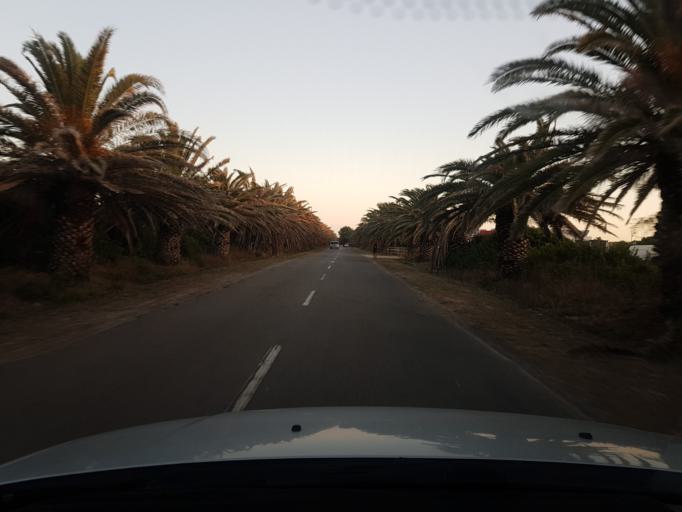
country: IT
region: Sardinia
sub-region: Provincia di Oristano
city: Riola Sardo
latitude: 40.0375
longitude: 8.4002
